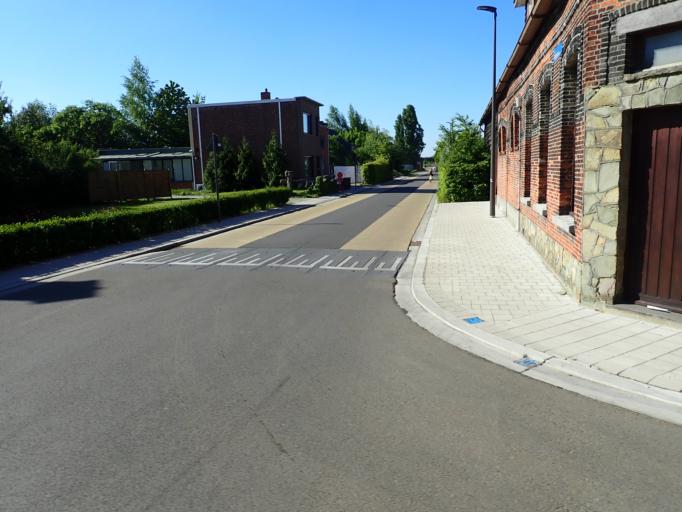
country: BE
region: Flanders
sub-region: Provincie Antwerpen
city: Wommelgem
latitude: 51.2081
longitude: 4.5301
